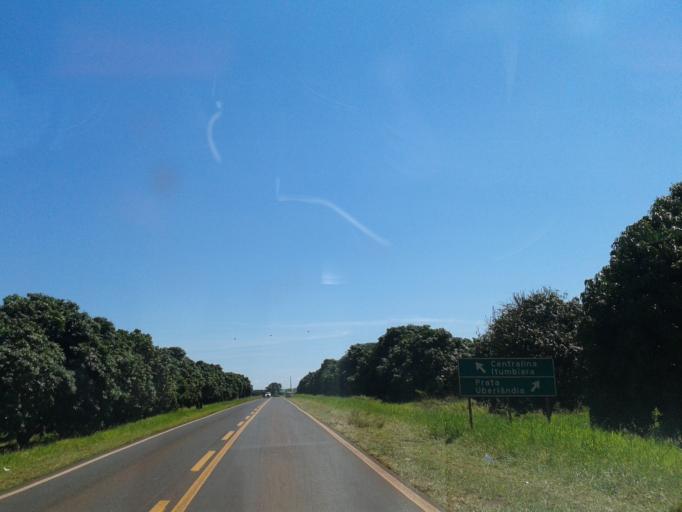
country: BR
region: Minas Gerais
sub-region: Centralina
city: Centralina
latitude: -18.7153
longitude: -49.1382
